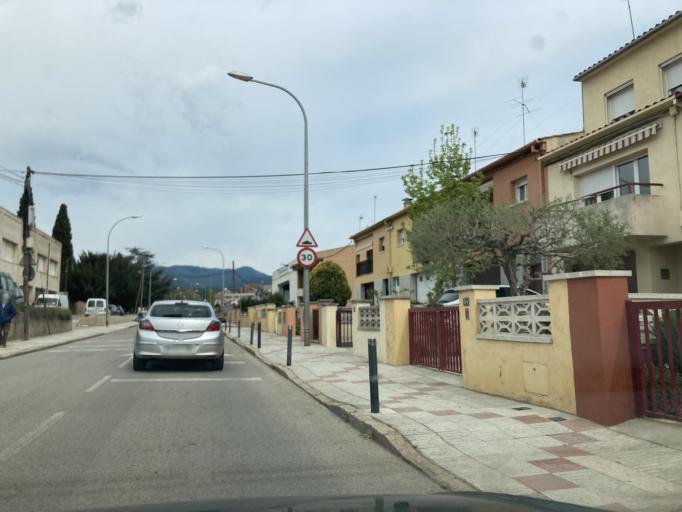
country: ES
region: Catalonia
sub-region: Provincia de Girona
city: Santa Coloma de Farners
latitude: 41.8651
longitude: 2.6589
